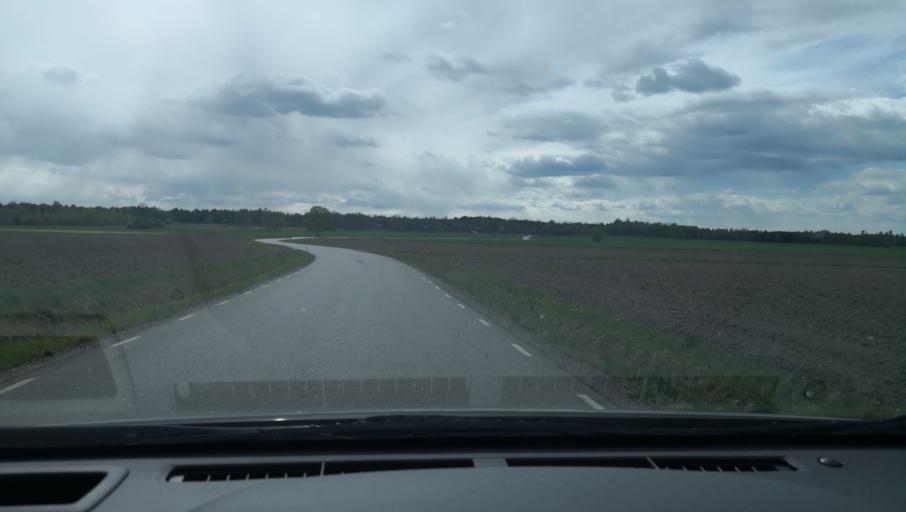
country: SE
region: OErebro
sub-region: Kumla Kommun
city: Hallabrottet
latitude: 59.1608
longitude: 15.2303
